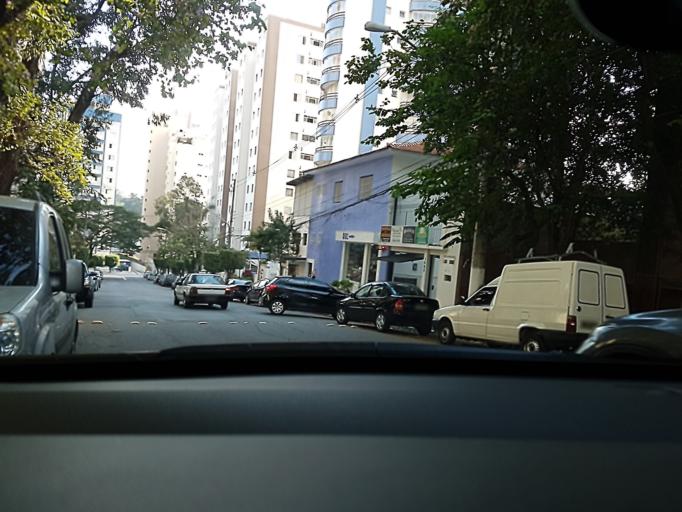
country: BR
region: Sao Paulo
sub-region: Diadema
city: Diadema
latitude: -23.6480
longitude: -46.6681
